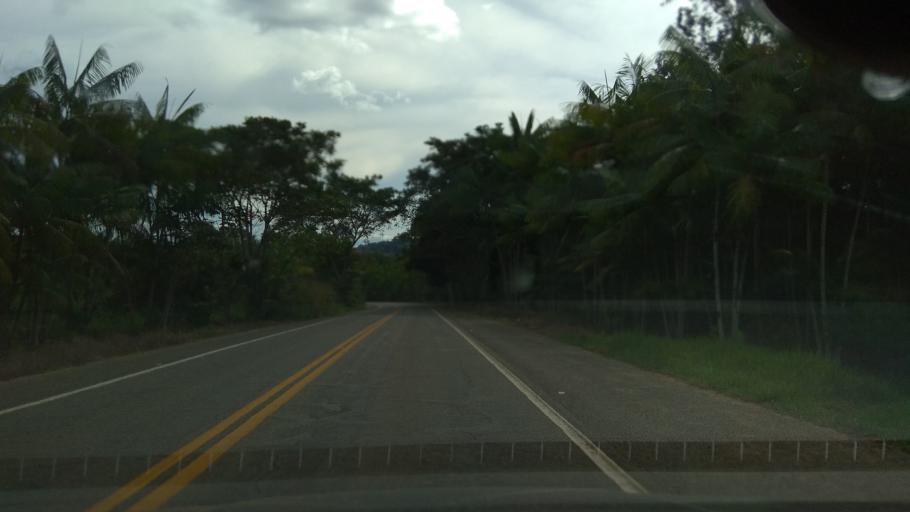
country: BR
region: Bahia
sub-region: Ubata
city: Ubata
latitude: -14.2298
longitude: -39.4365
